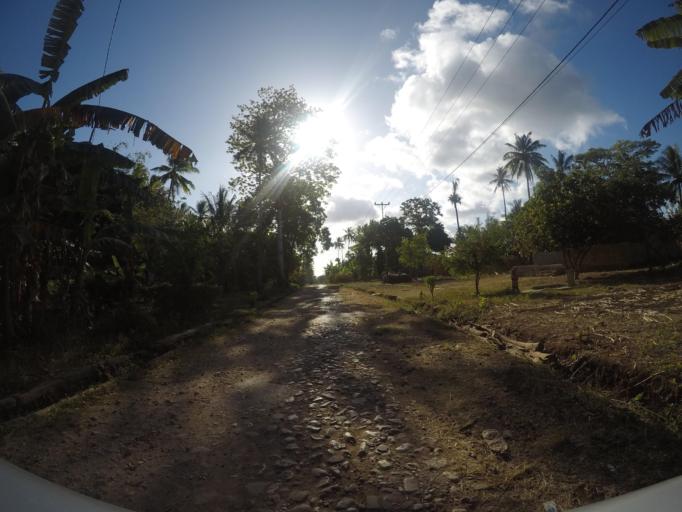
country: TL
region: Lautem
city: Lospalos
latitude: -8.4440
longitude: 126.8685
